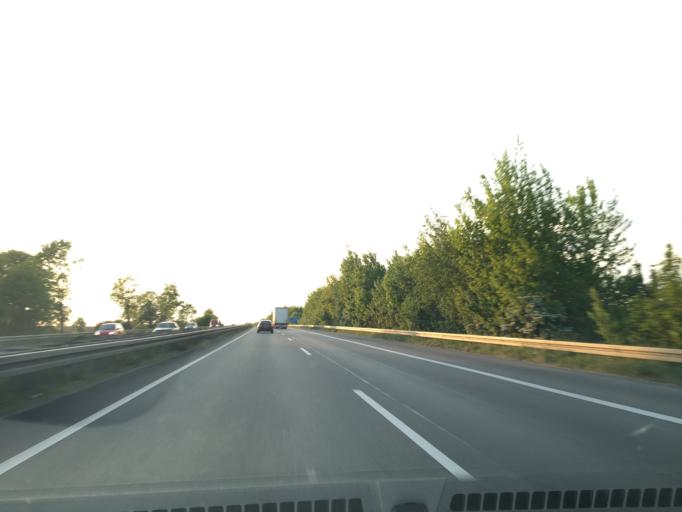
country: DE
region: Lower Saxony
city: Melle
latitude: 52.2008
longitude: 8.3096
